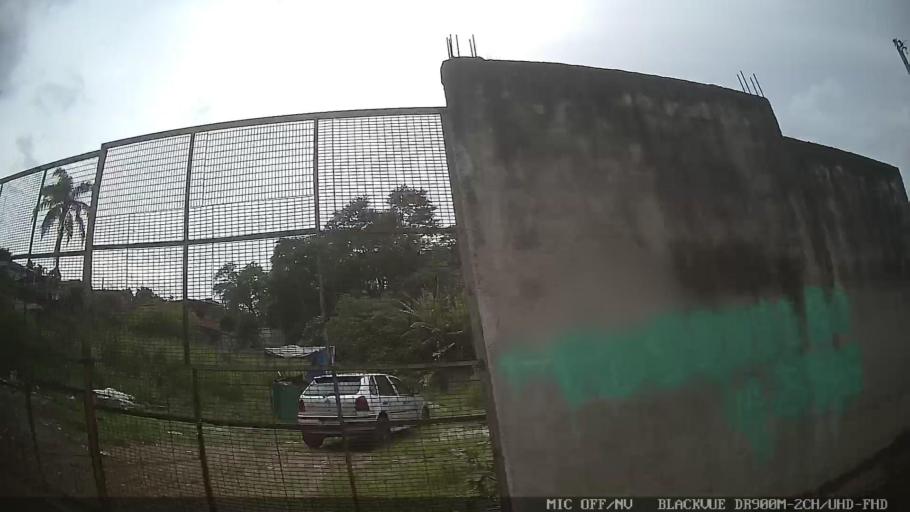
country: BR
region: Sao Paulo
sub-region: Itaquaquecetuba
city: Itaquaquecetuba
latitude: -23.4532
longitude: -46.3036
